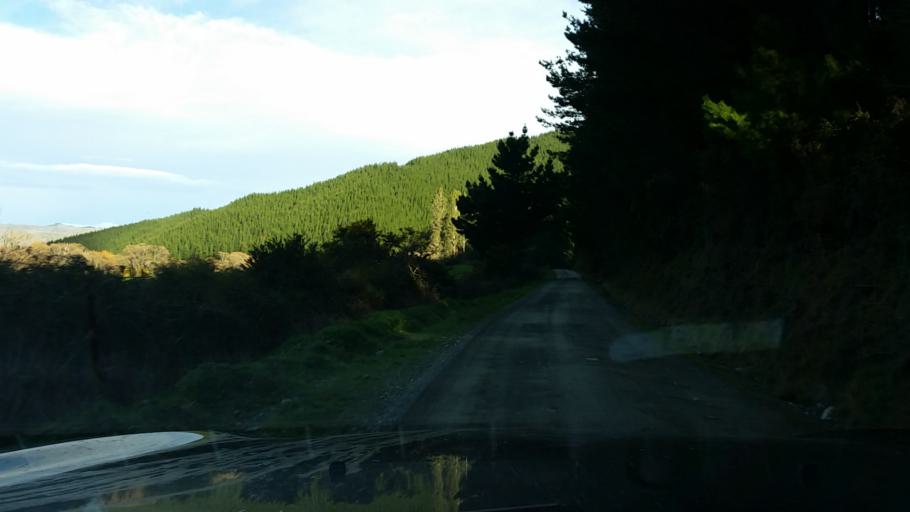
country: NZ
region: Nelson
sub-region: Nelson City
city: Nelson
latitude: -41.5563
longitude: 173.4295
